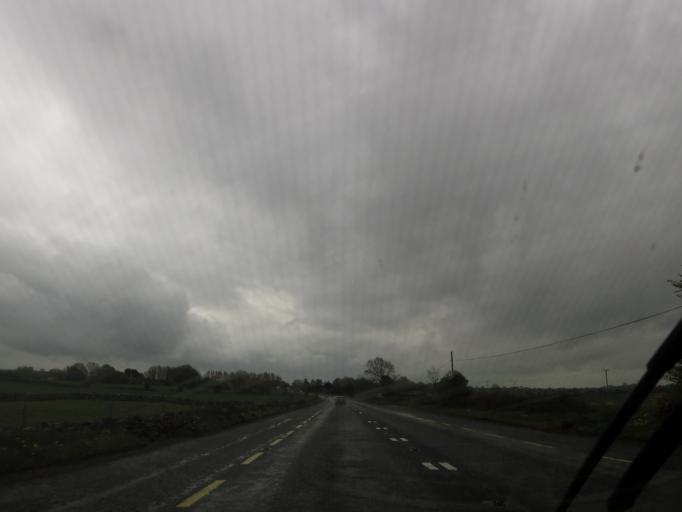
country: IE
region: Connaught
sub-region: County Galway
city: Claregalway
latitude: 53.4079
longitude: -8.9105
